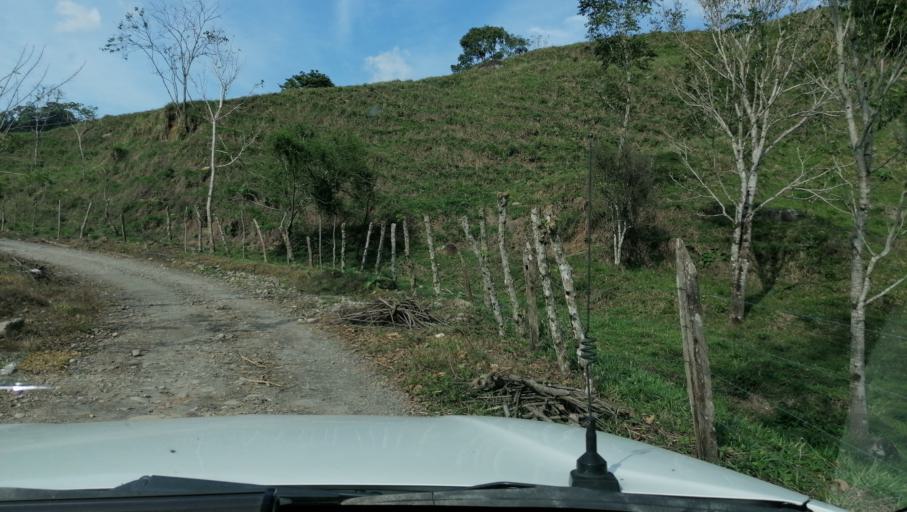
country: MX
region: Chiapas
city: Ostuacan
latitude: 17.4589
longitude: -93.2408
